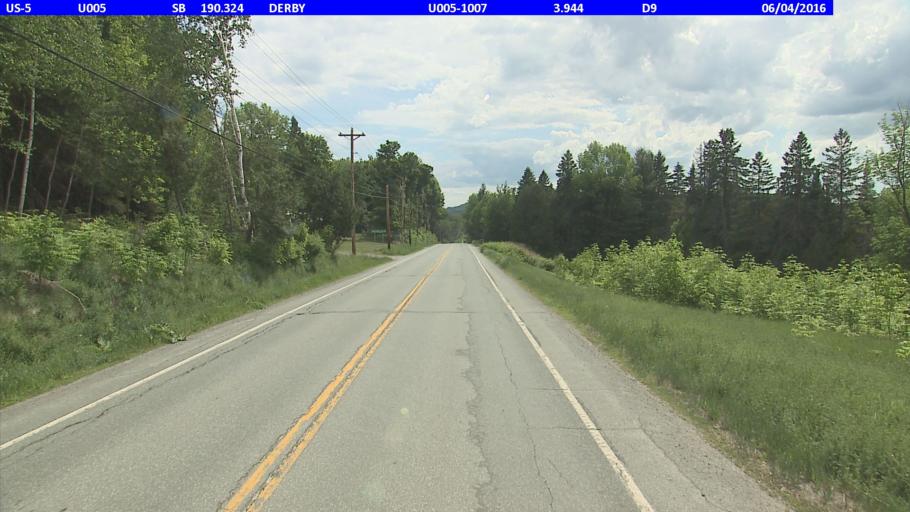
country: US
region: Vermont
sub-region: Orleans County
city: Newport
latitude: 44.9793
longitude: -72.1126
